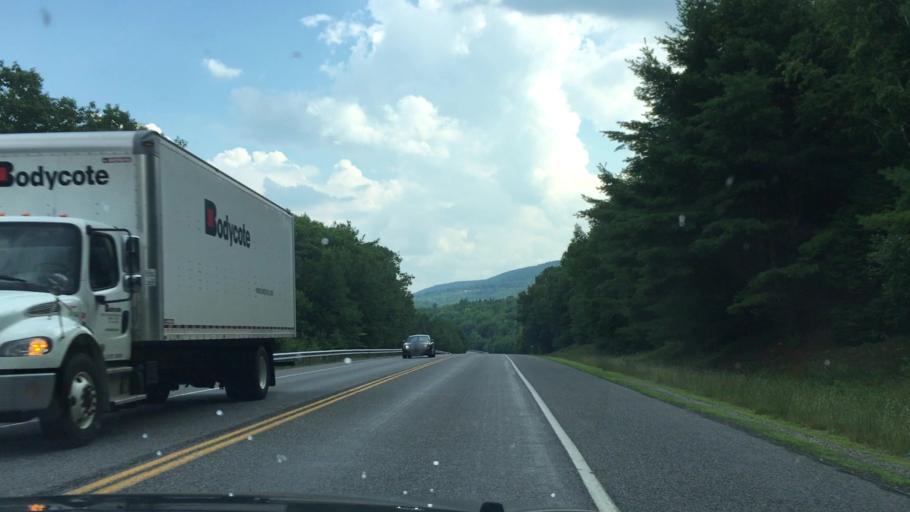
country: US
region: New Hampshire
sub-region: Carroll County
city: Wolfeboro
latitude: 43.5093
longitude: -71.2661
